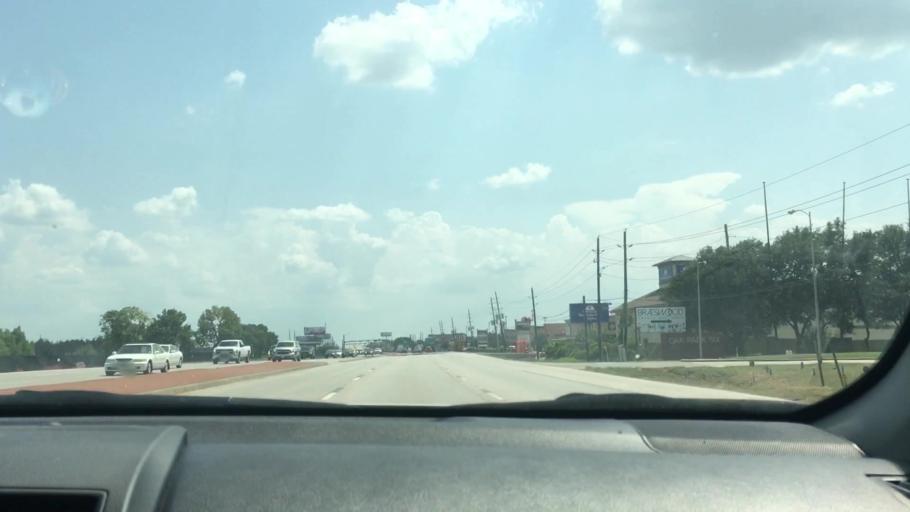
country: US
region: Texas
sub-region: Fort Bend County
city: Mission Bend
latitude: 29.7244
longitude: -95.6441
